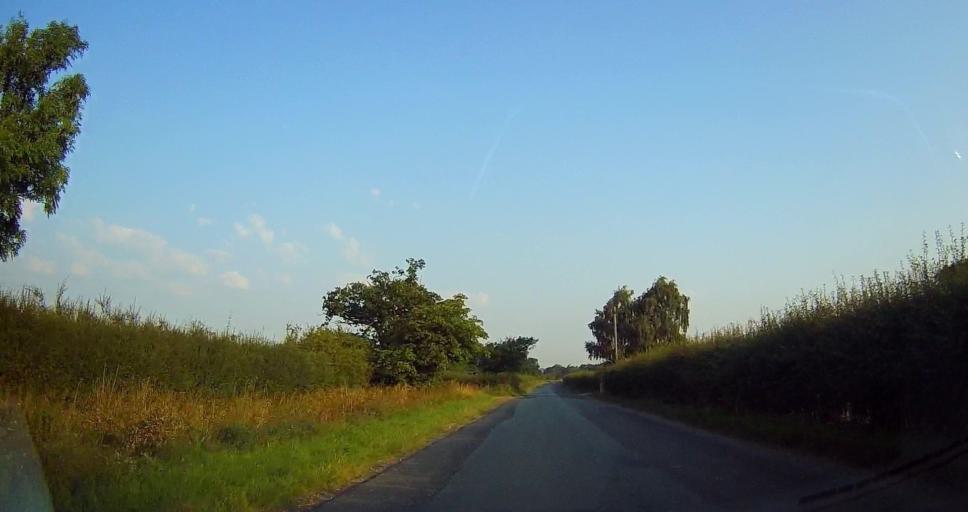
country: GB
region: England
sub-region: Cheshire East
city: Nantwich
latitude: 53.0393
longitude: -2.5163
